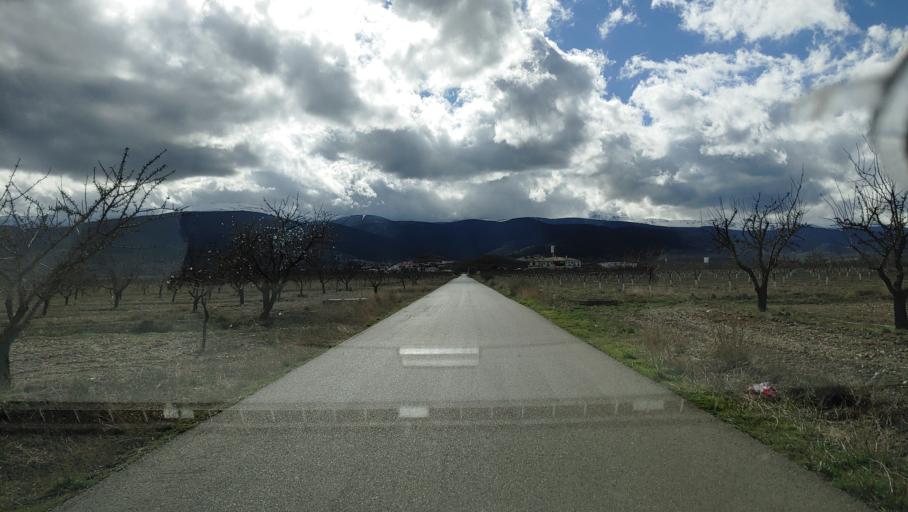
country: ES
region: Andalusia
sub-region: Provincia de Granada
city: Hueneja
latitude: 37.1991
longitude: -2.9812
